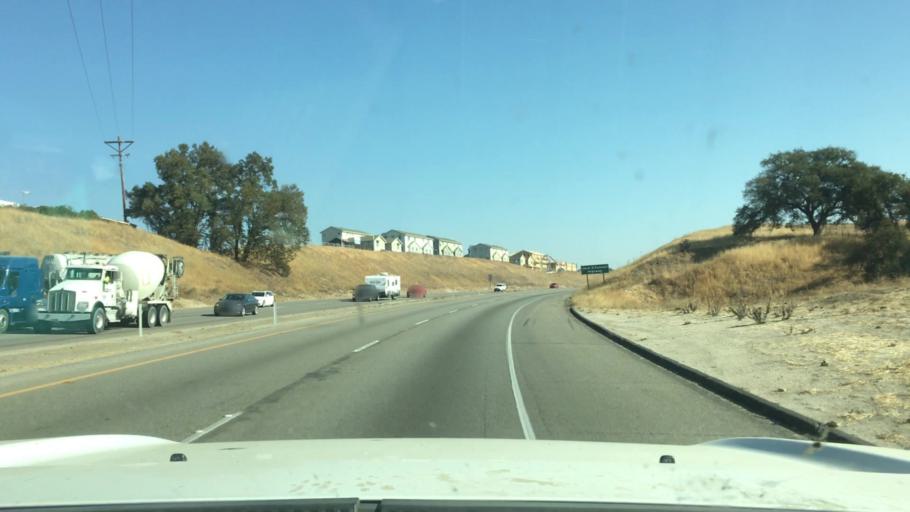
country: US
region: California
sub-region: San Luis Obispo County
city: Paso Robles
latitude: 35.6441
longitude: -120.6804
